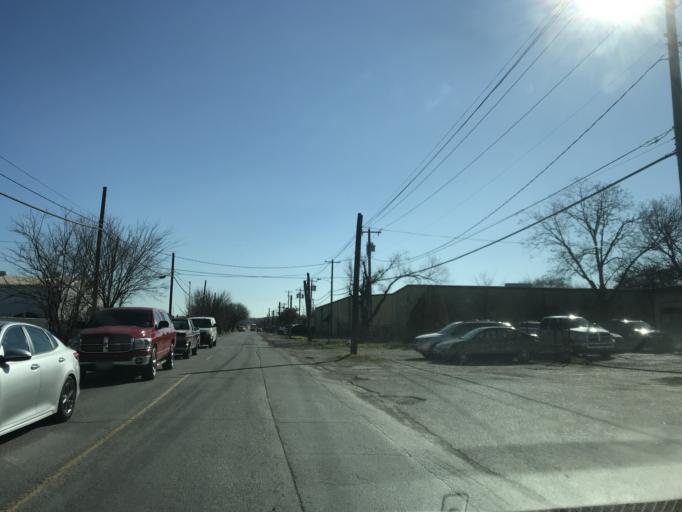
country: US
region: Texas
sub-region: Dallas County
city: Cockrell Hill
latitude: 32.7782
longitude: -96.9055
